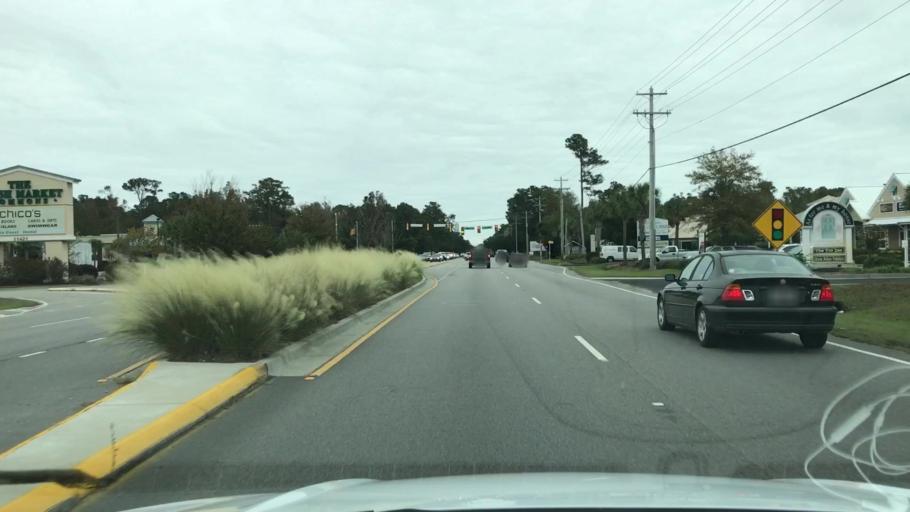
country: US
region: South Carolina
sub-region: Georgetown County
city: Murrells Inlet
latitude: 33.4493
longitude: -79.1197
